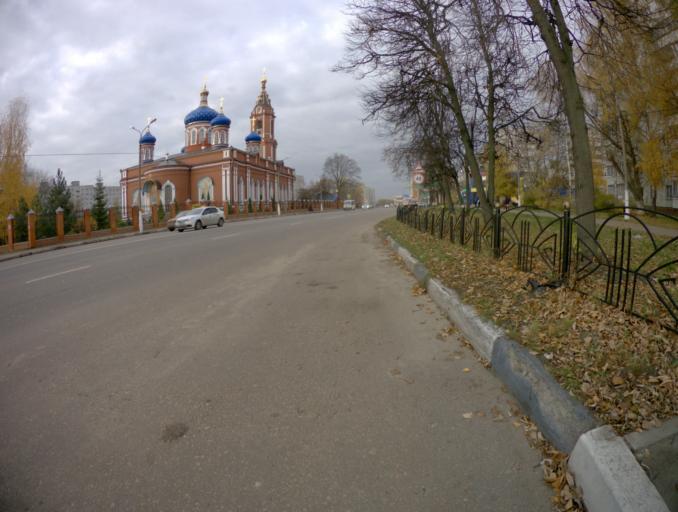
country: RU
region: Moskovskaya
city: Orekhovo-Zuyevo
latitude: 55.8083
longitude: 38.9622
